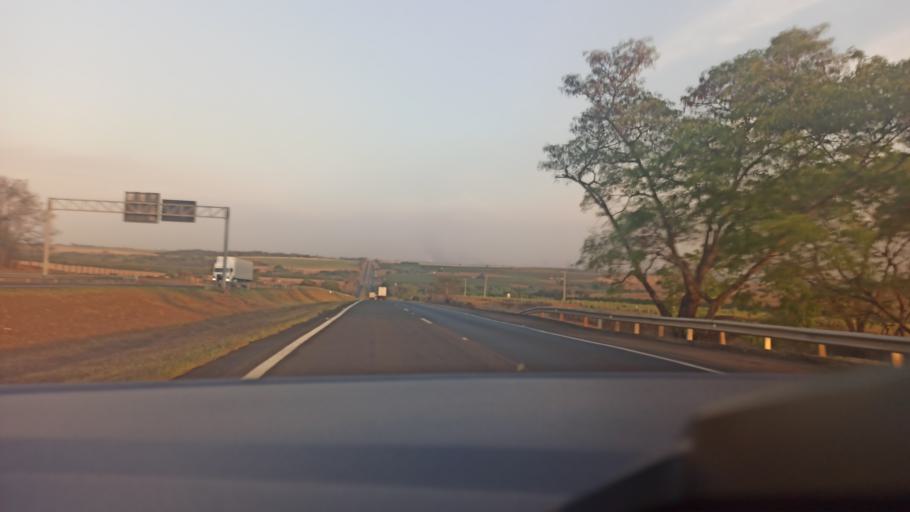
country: BR
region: Sao Paulo
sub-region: Santa Adelia
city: Santa Adelia
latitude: -21.3884
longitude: -48.7246
